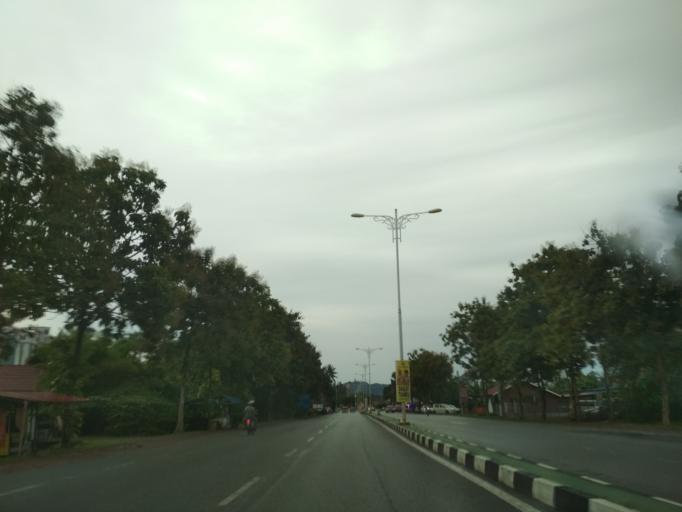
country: MY
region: Perlis
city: Kangar
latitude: 6.4419
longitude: 100.2066
